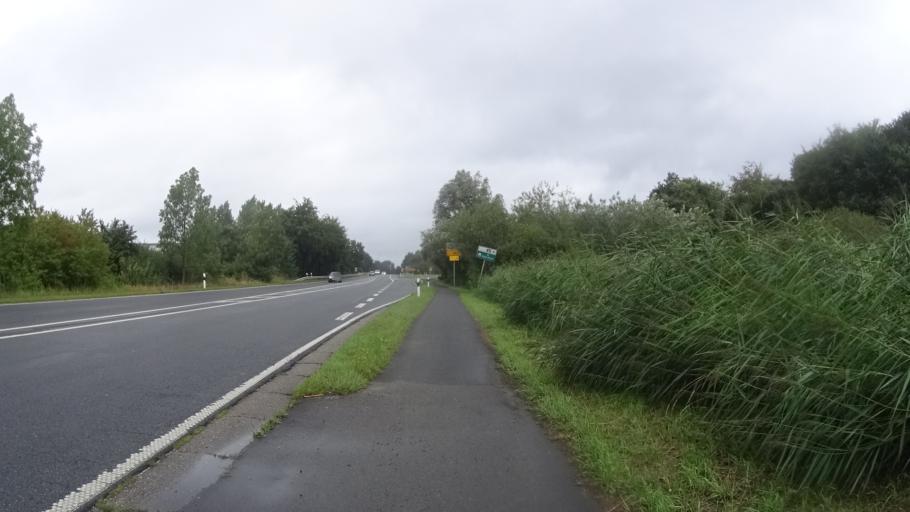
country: DE
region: Lower Saxony
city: Leer
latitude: 53.2272
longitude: 7.4363
